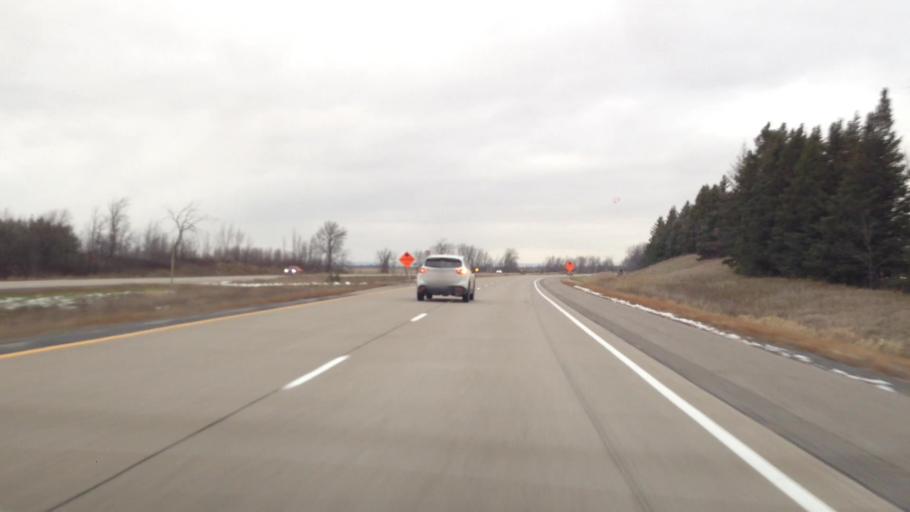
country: CA
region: Ontario
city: Hawkesbury
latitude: 45.4103
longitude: -74.7706
